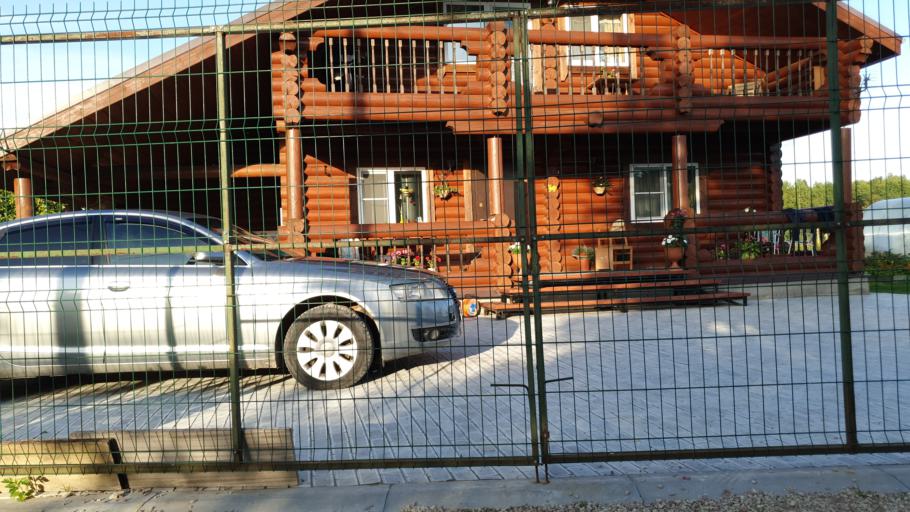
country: RU
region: Leningrad
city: Ivangorod
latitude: 59.4287
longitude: 28.3228
